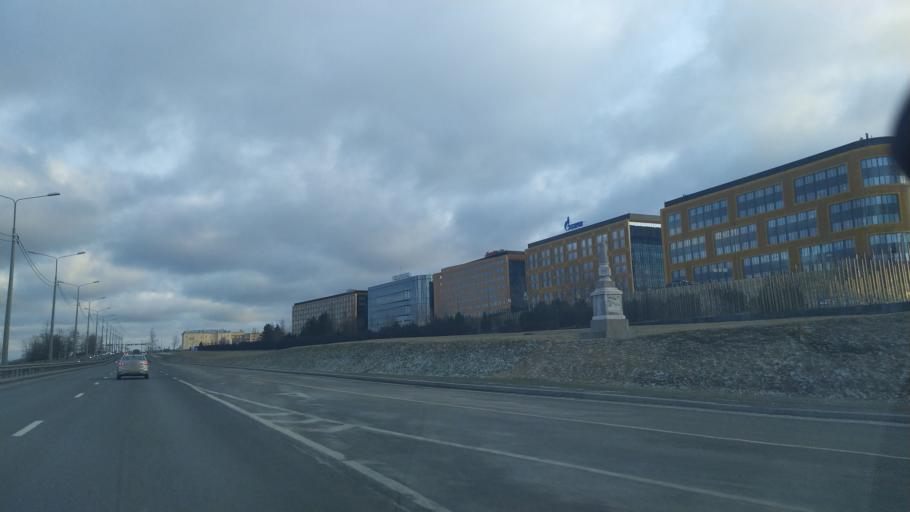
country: RU
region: St.-Petersburg
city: Aleksandrovskaya
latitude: 59.7660
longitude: 30.3534
